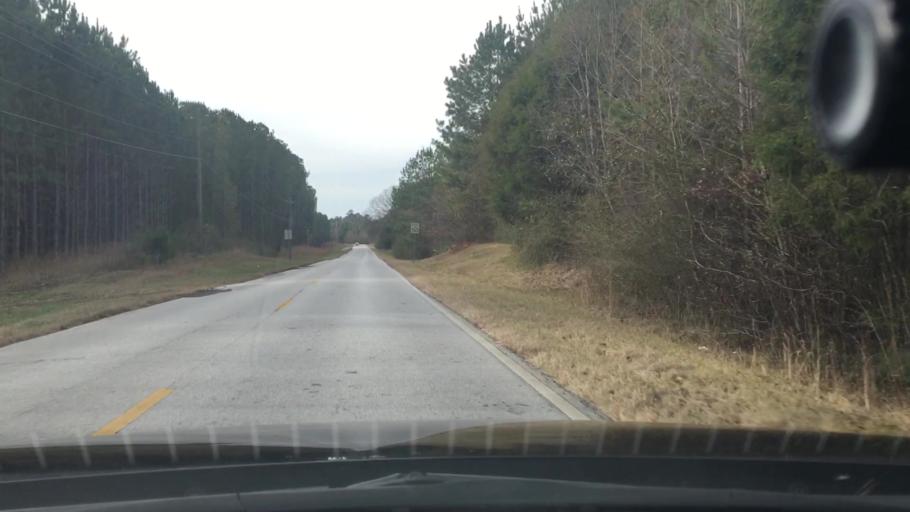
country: US
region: Georgia
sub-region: Spalding County
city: Experiment
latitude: 33.2706
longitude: -84.3459
